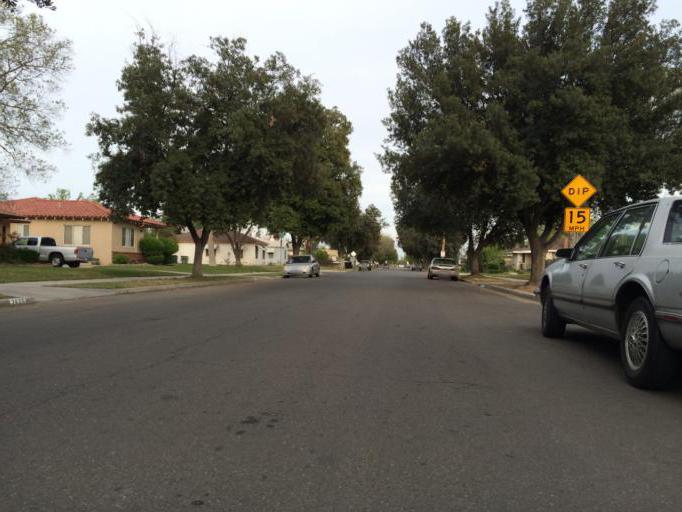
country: US
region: California
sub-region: Fresno County
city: Fresno
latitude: 36.7759
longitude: -119.7778
